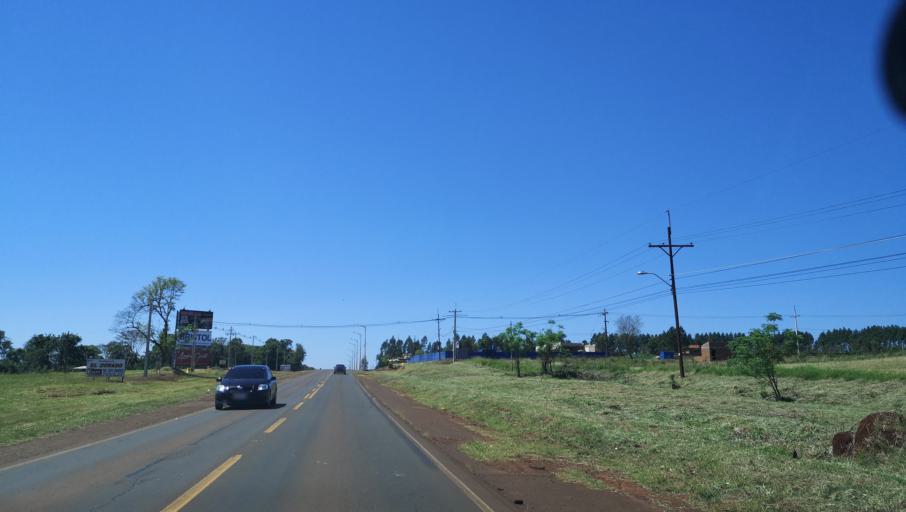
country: PY
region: Itapua
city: San Juan del Parana
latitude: -27.2722
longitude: -55.9537
